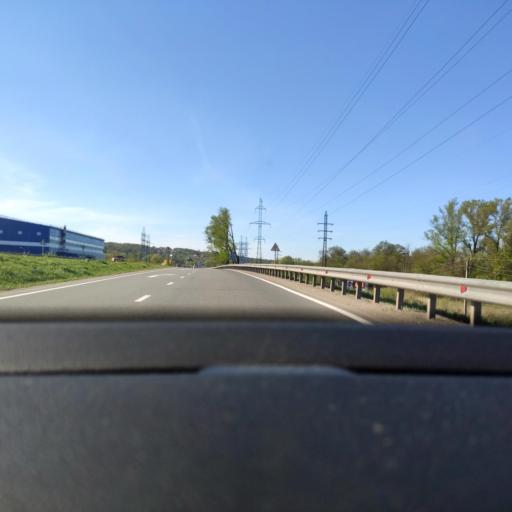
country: RU
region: Moskovskaya
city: Yakhroma
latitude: 56.2947
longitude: 37.4877
